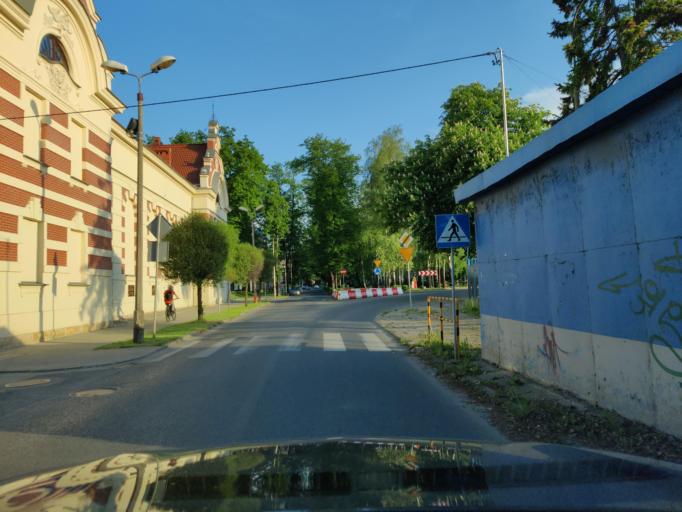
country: PL
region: Silesian Voivodeship
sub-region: Powiat zywiecki
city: Zywiec
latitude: 49.6901
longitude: 19.1943
